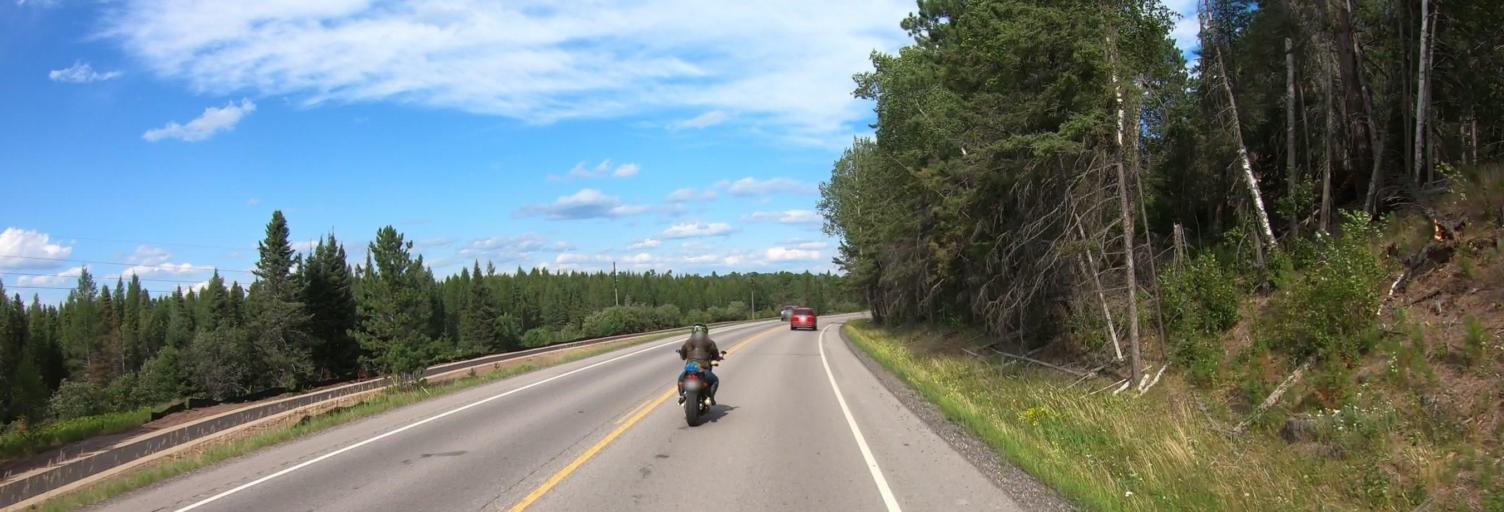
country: US
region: Minnesota
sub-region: Saint Louis County
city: Ely
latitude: 47.8907
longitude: -91.9378
